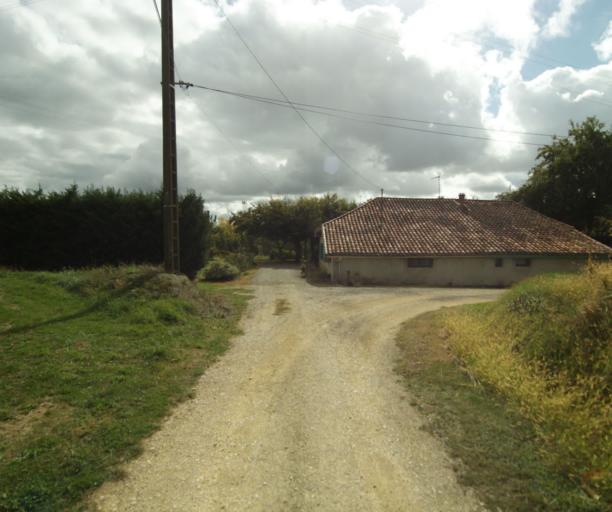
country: FR
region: Midi-Pyrenees
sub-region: Departement du Gers
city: Nogaro
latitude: 43.8462
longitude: -0.0230
